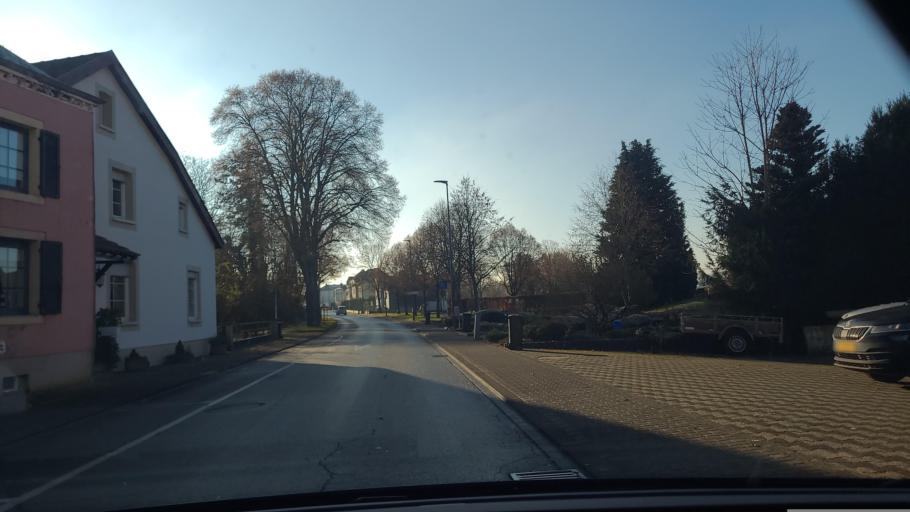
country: LU
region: Luxembourg
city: Hautcharage
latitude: 49.5738
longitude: 5.9091
